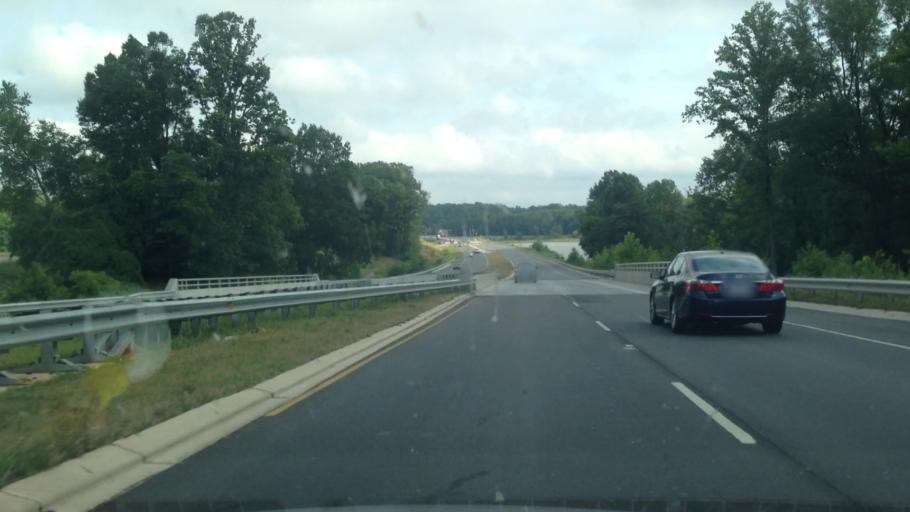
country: US
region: North Carolina
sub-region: Guilford County
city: Summerfield
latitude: 36.1679
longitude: -79.8791
